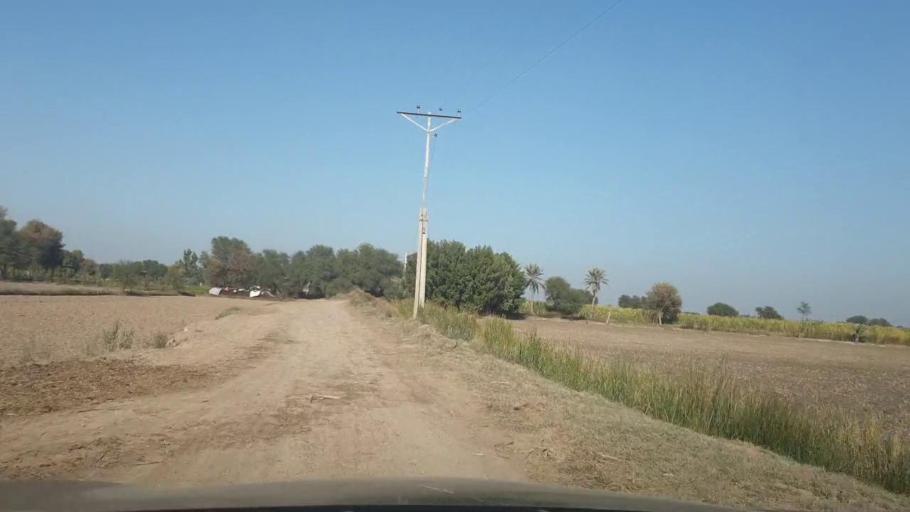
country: PK
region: Sindh
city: Mirpur Mathelo
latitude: 28.1411
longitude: 69.5968
